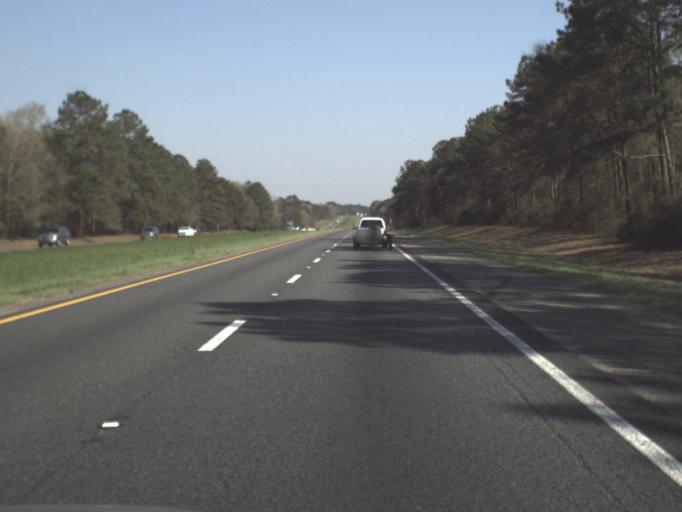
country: US
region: Florida
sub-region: Gadsden County
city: Gretna
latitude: 30.5683
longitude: -84.6664
